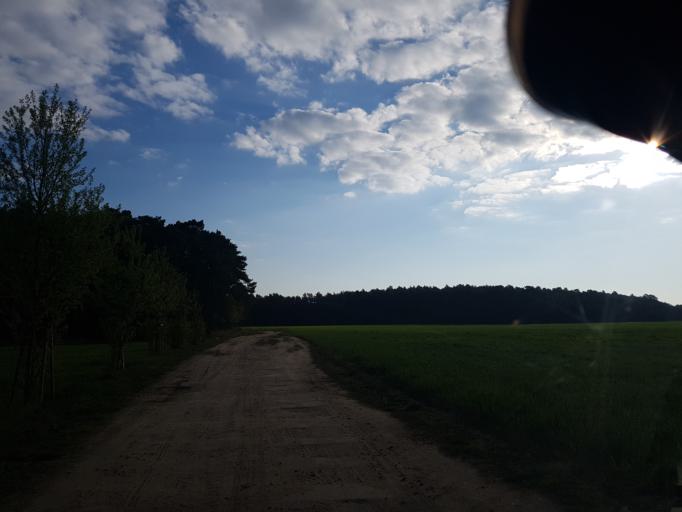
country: DE
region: Brandenburg
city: Treuenbrietzen
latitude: 52.1092
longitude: 12.8323
